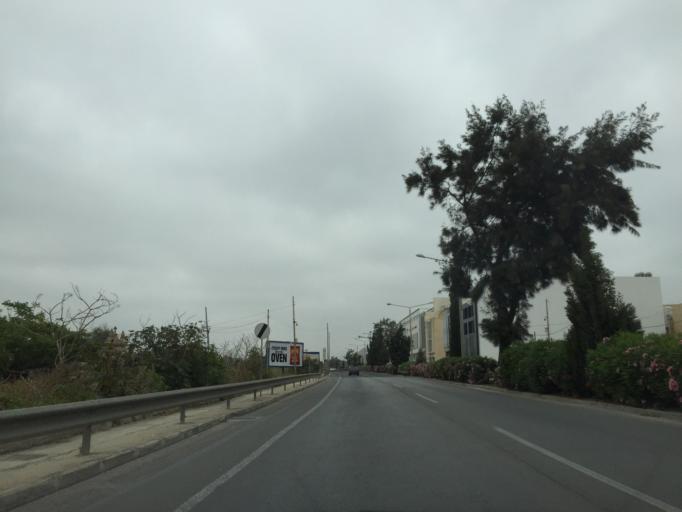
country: MT
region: Saint Venera
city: Santa Venera
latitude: 35.8875
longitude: 14.4654
